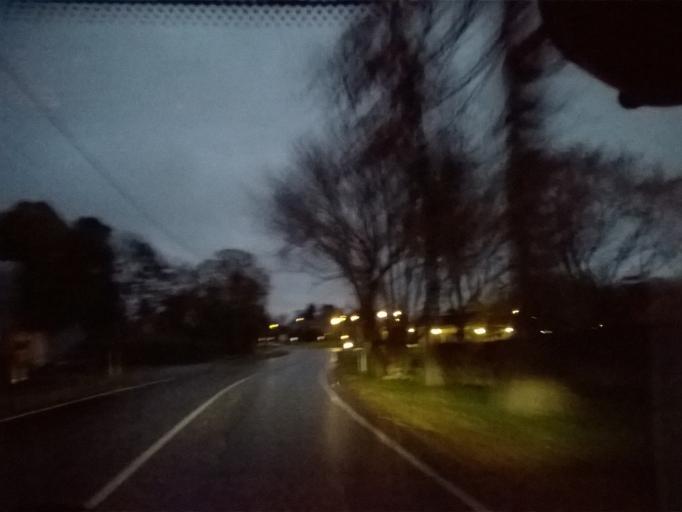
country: EE
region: Harju
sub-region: Viimsi vald
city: Viimsi
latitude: 59.5149
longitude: 24.8488
